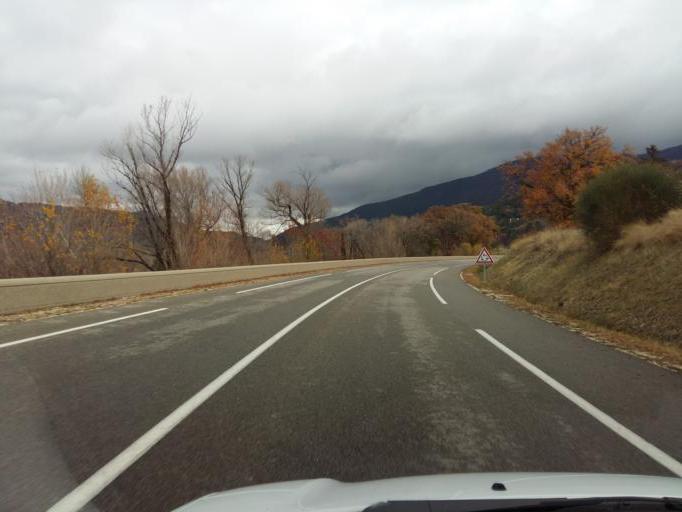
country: FR
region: Rhone-Alpes
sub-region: Departement de la Drome
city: Nyons
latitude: 44.3519
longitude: 5.1272
